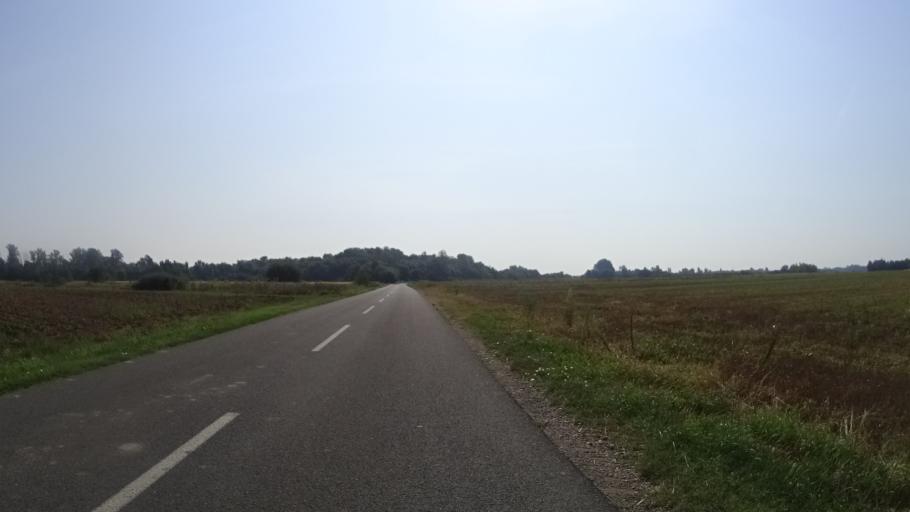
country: HR
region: Medimurska
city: Belica
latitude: 46.3952
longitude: 16.5250
